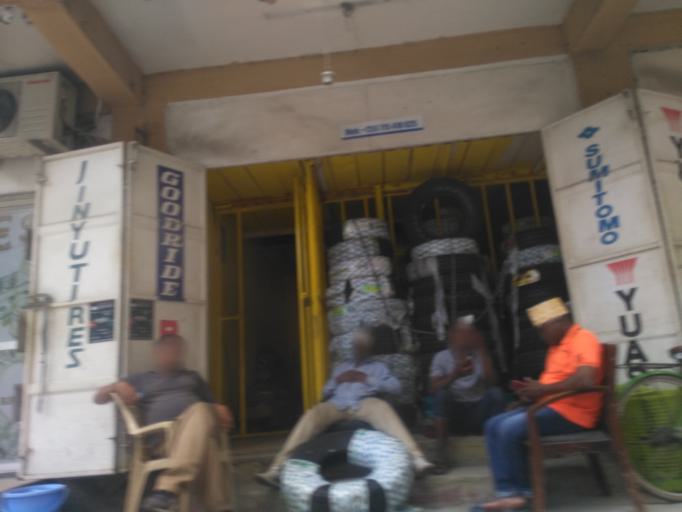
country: TZ
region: Dar es Salaam
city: Dar es Salaam
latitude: -6.8180
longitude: 39.2772
